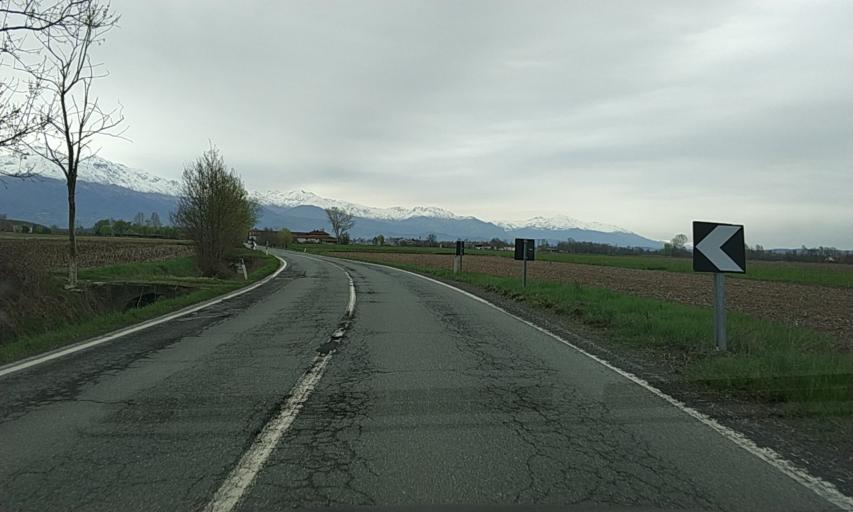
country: IT
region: Piedmont
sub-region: Provincia di Torino
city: Front
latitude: 45.3034
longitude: 7.6774
